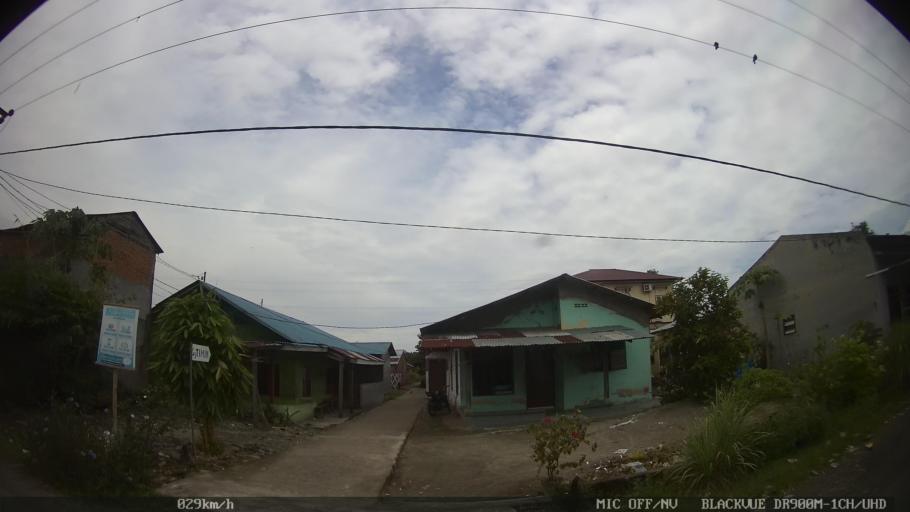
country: ID
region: North Sumatra
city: Sunggal
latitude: 3.6272
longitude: 98.5904
